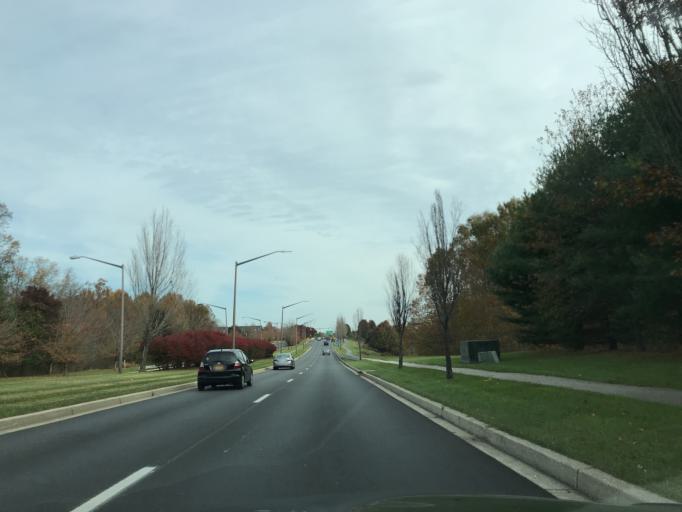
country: US
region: Maryland
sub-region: Howard County
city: Columbia
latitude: 39.2080
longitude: -76.8046
